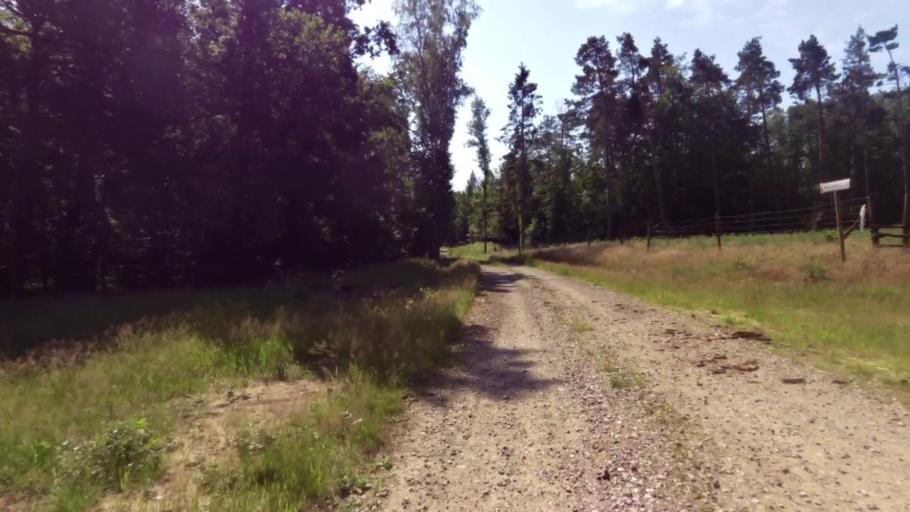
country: PL
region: West Pomeranian Voivodeship
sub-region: Powiat swidwinski
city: Polczyn-Zdroj
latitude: 53.8508
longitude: 16.1406
